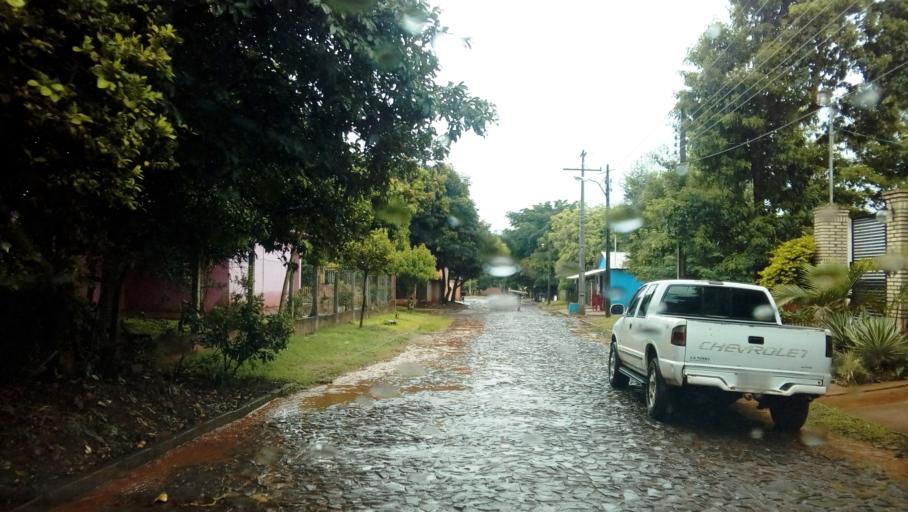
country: PY
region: Alto Parana
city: Ciudad del Este
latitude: -25.4212
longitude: -54.6422
